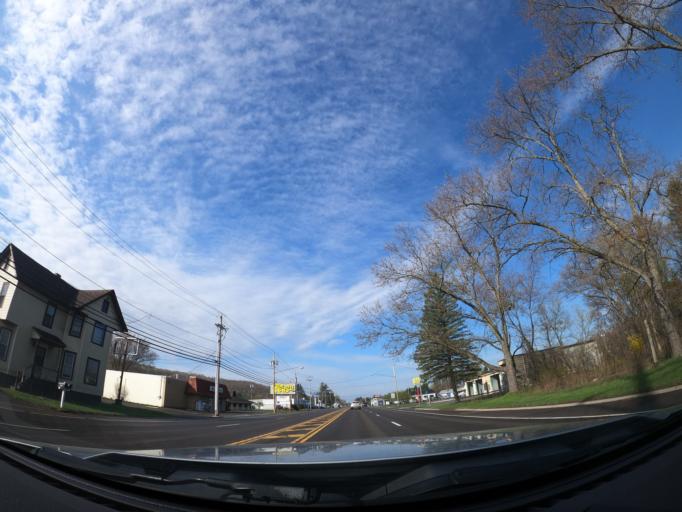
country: US
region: New York
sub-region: Cortland County
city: Munsons Corners
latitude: 42.5855
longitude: -76.2002
